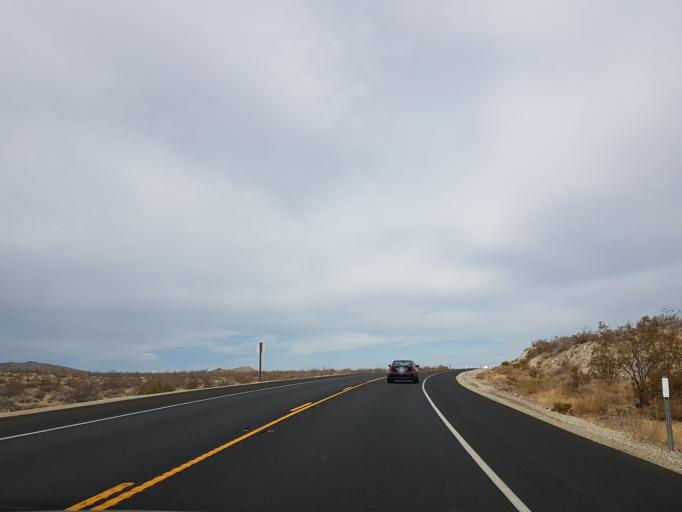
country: US
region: California
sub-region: Kern County
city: Ridgecrest
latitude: 35.4602
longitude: -117.6554
